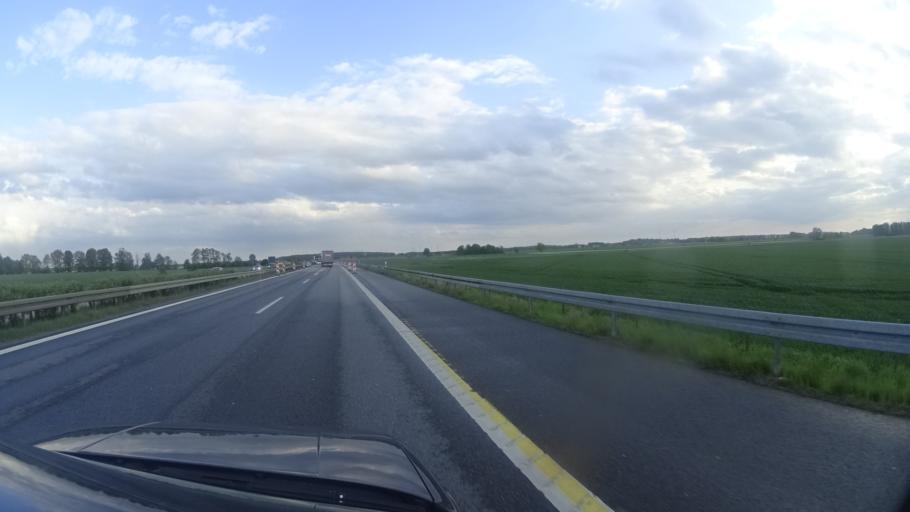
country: DE
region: Brandenburg
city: Wittstock
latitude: 53.2541
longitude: 12.4475
